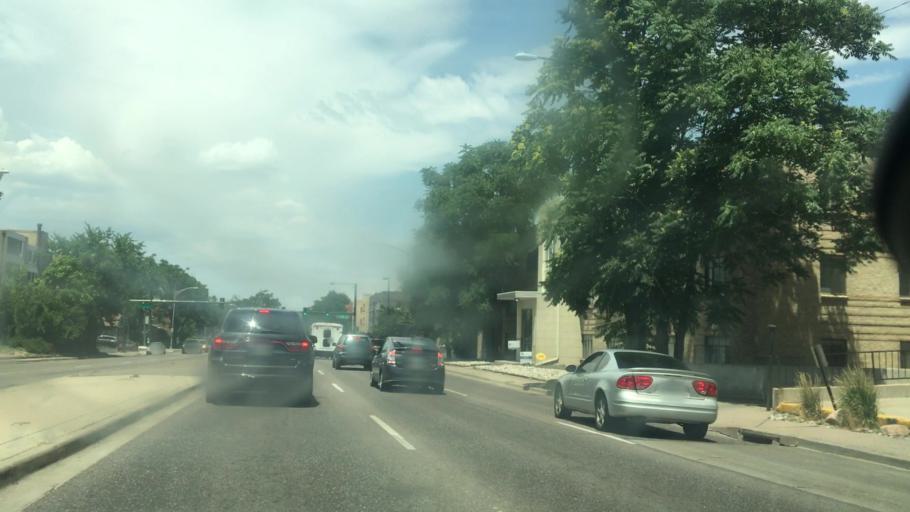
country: US
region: Colorado
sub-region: Arapahoe County
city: Glendale
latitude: 39.7336
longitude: -104.9406
